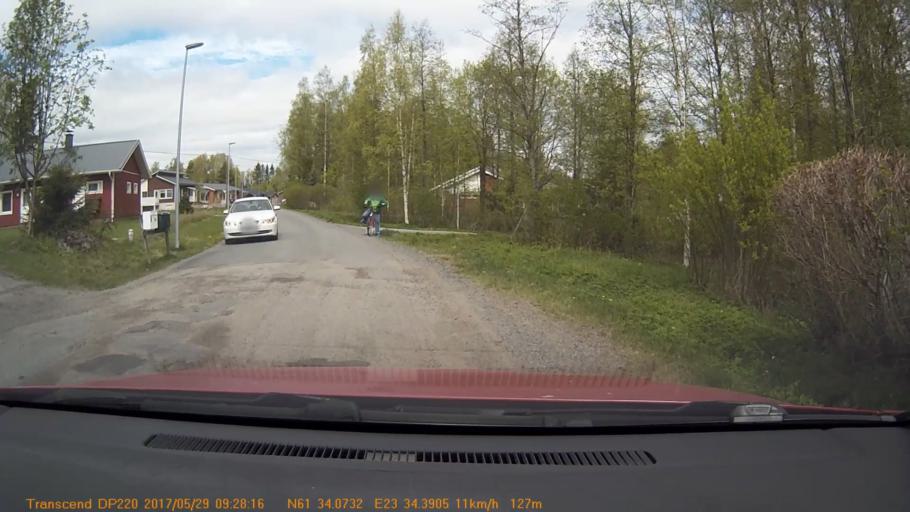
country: FI
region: Pirkanmaa
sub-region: Tampere
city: Yloejaervi
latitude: 61.5678
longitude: 23.5732
